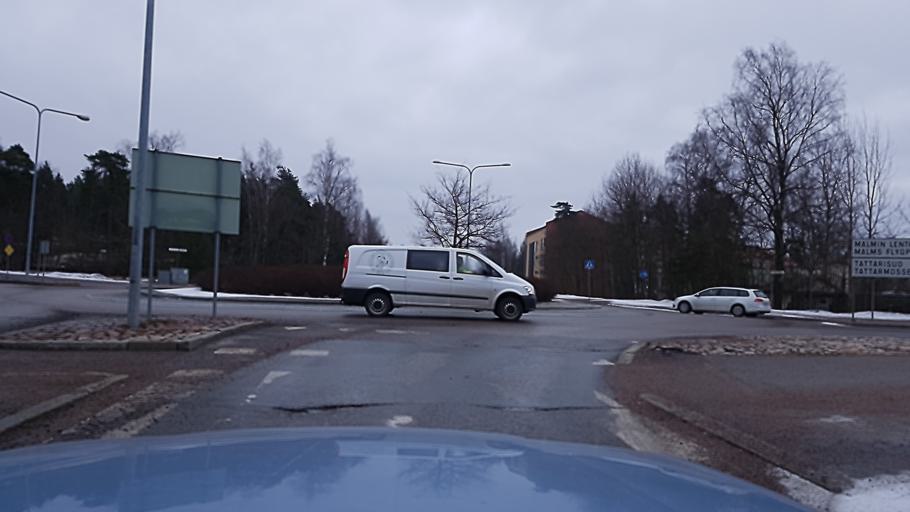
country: FI
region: Uusimaa
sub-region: Helsinki
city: Vantaa
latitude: 60.2632
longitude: 25.0683
